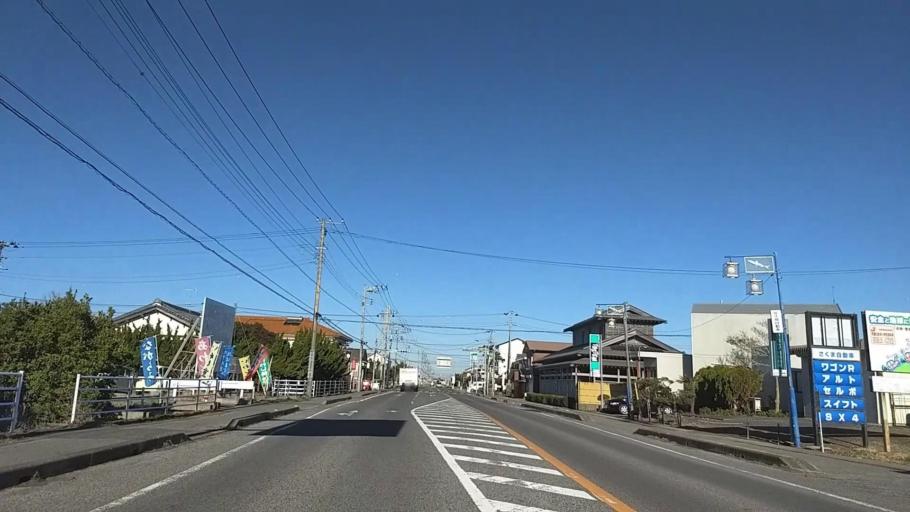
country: JP
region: Chiba
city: Togane
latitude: 35.5079
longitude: 140.4333
